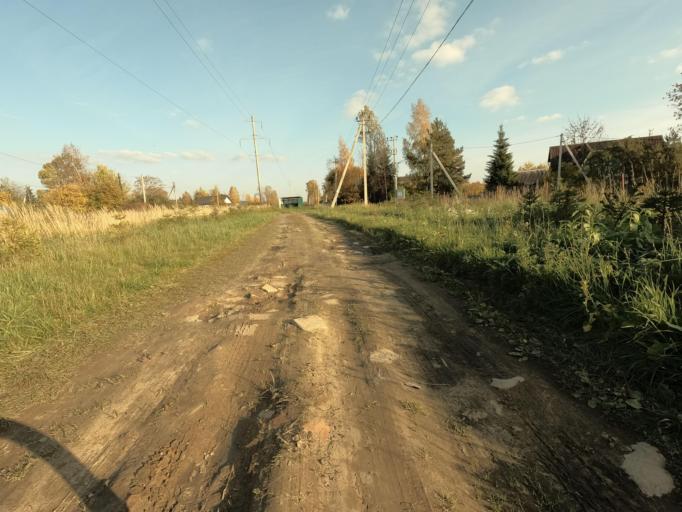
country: RU
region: Leningrad
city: Mga
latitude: 59.7508
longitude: 31.0579
